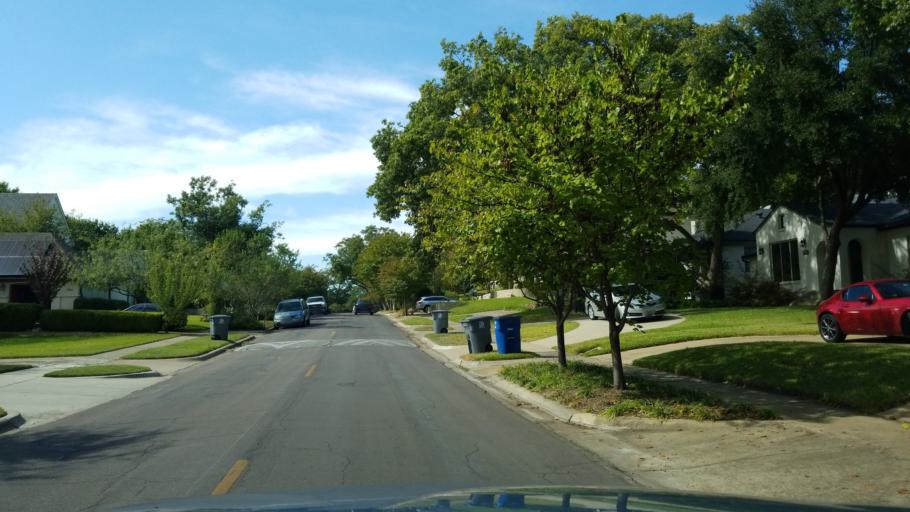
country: US
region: Texas
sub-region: Dallas County
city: Highland Park
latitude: 32.8114
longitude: -96.7416
